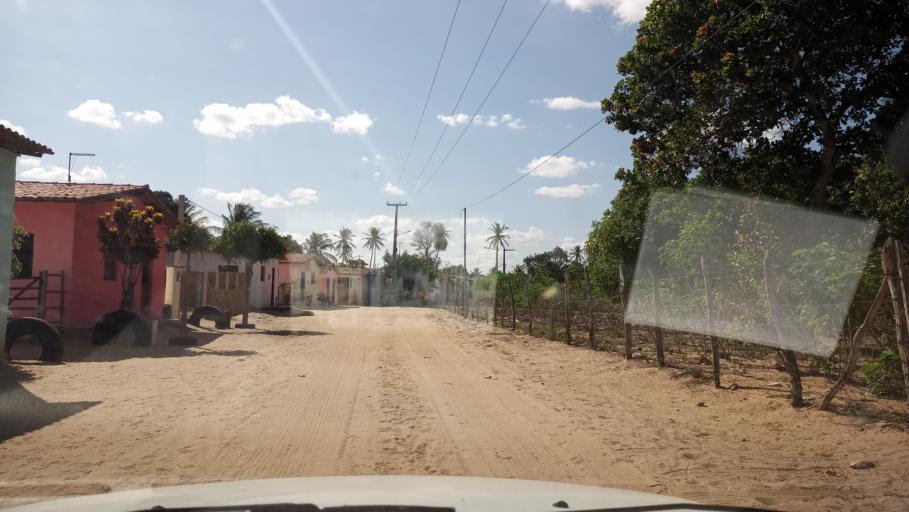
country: BR
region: Rio Grande do Norte
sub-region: Brejinho
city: Brejinho
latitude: -6.1745
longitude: -35.4665
